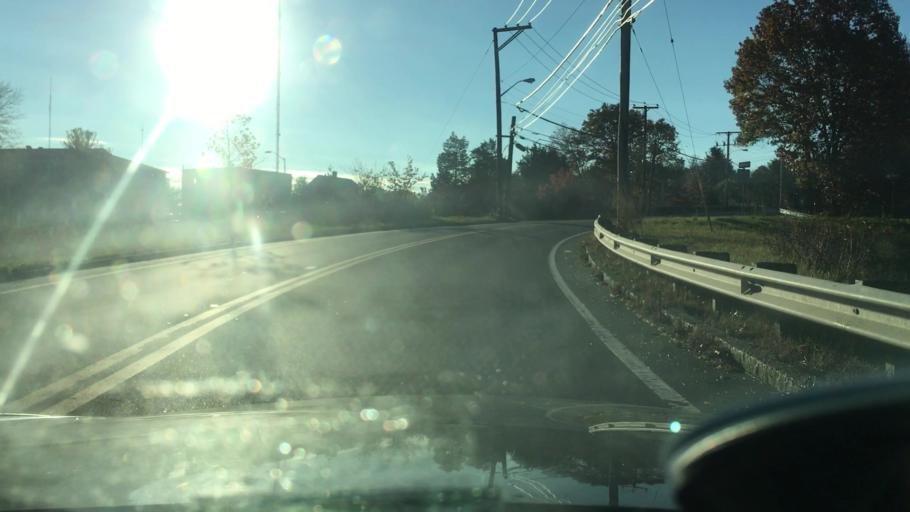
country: US
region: Massachusetts
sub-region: Norfolk County
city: Needham
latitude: 42.3172
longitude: -71.2472
